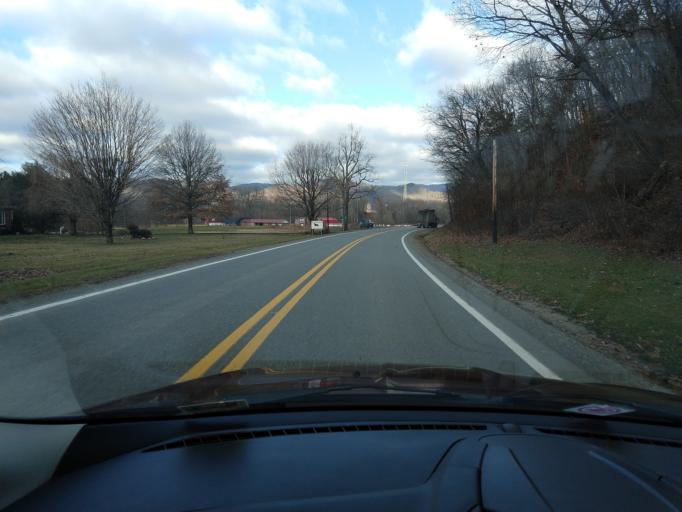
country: US
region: West Virginia
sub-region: Randolph County
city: Elkins
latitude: 38.6825
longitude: -79.9721
